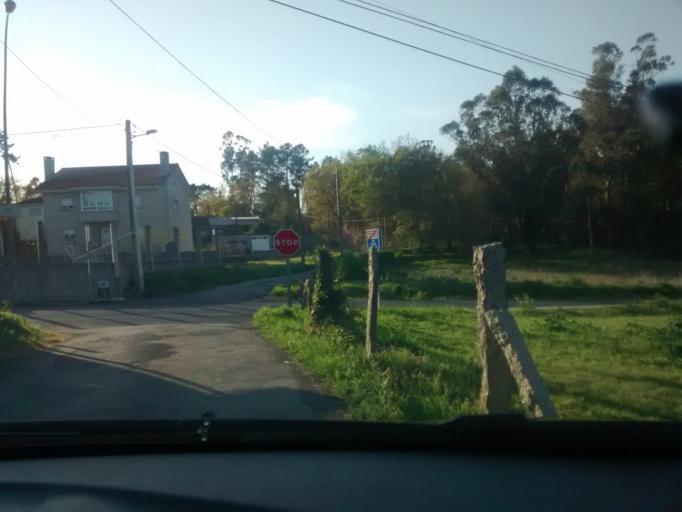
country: ES
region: Galicia
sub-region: Provincia de Pontevedra
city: A Estrada
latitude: 42.6966
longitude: -8.4827
